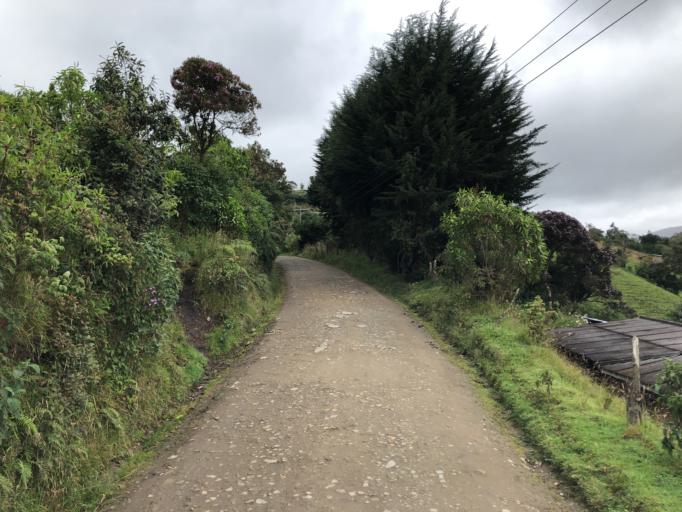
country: CO
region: Cauca
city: Totoro
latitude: 2.4964
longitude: -76.3464
